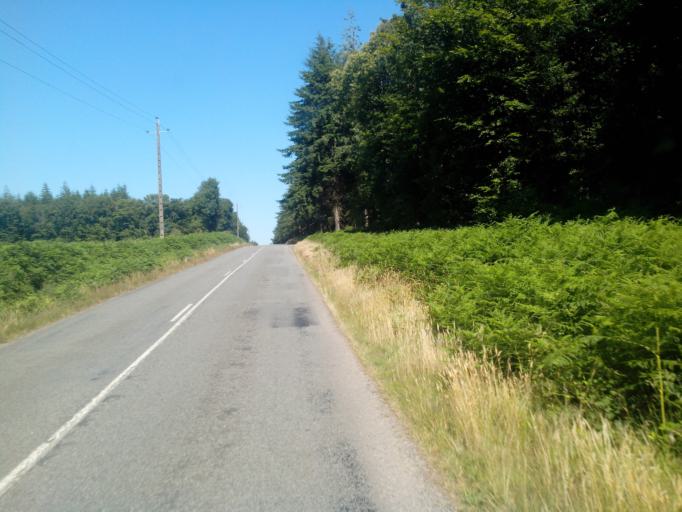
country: FR
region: Brittany
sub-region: Departement d'Ille-et-Vilaine
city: Paimpont
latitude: 48.0069
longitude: -2.2139
